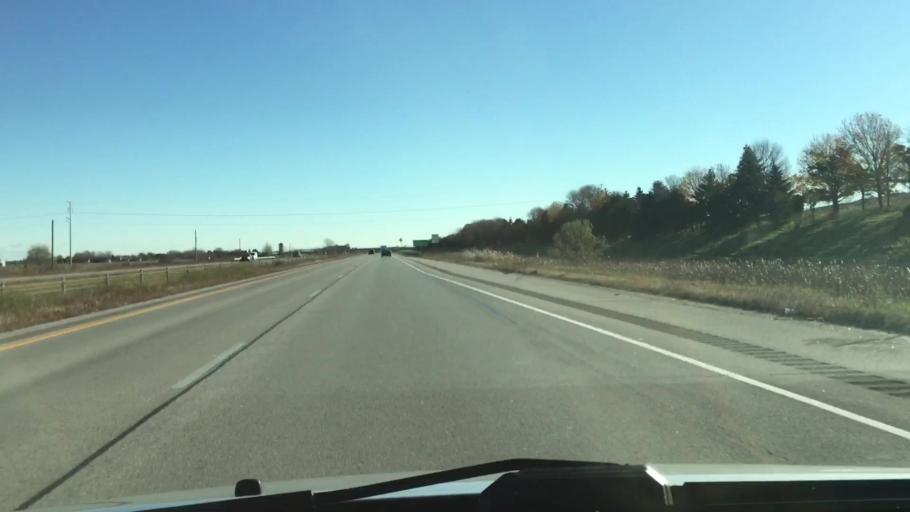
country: US
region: Wisconsin
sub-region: Outagamie County
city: Kimberly
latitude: 44.2979
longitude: -88.3488
